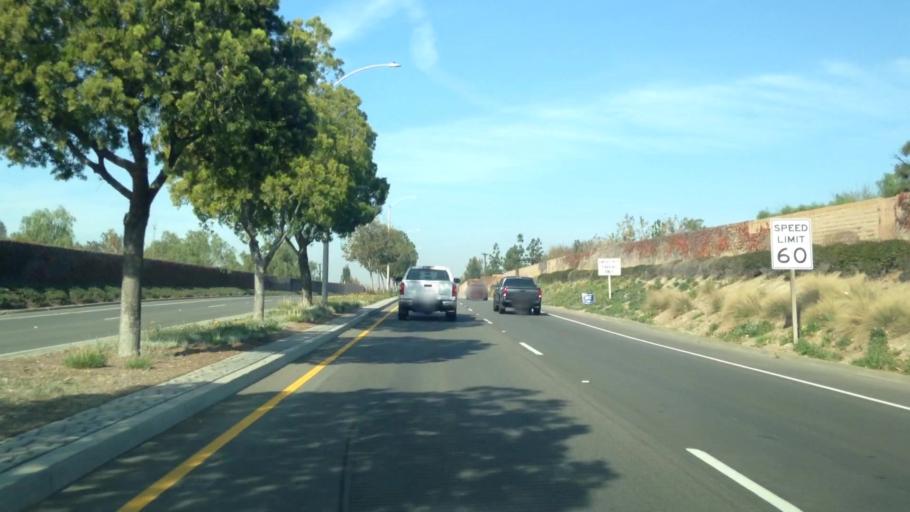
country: US
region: California
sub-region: Orange County
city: Yorba Linda
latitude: 33.8787
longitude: -117.8079
